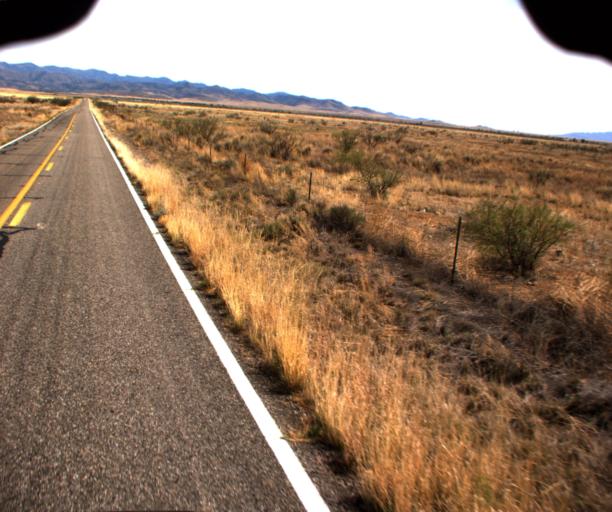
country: US
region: Arizona
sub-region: Cochise County
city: Willcox
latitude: 32.0495
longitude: -109.4904
